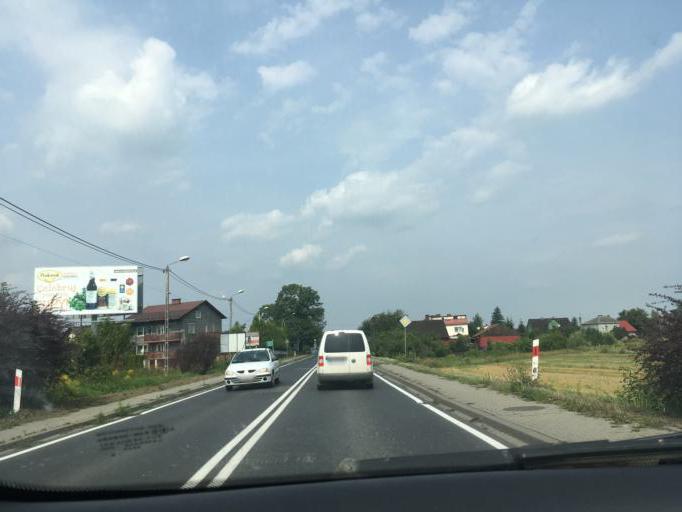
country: PL
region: Lesser Poland Voivodeship
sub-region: Powiat oswiecimski
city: Babice
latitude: 50.0495
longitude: 19.2047
